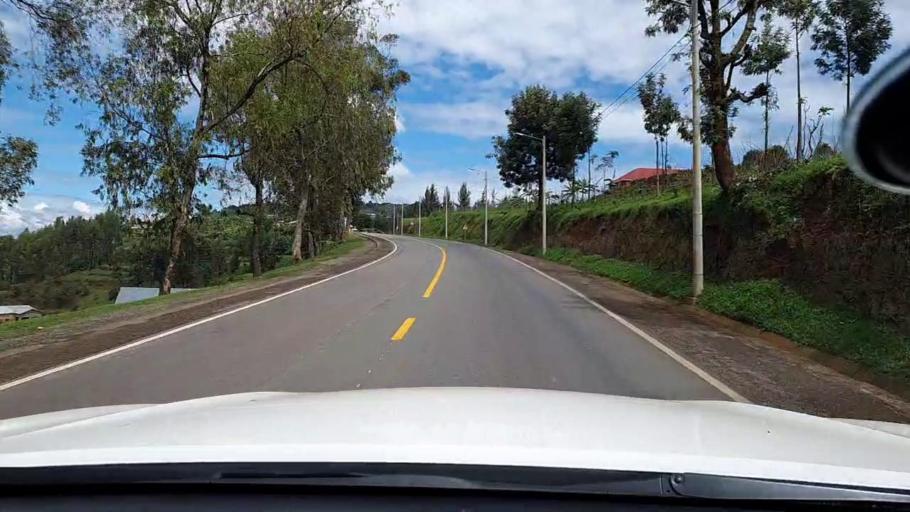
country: RW
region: Kigali
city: Kigali
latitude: -1.8382
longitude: 29.9538
